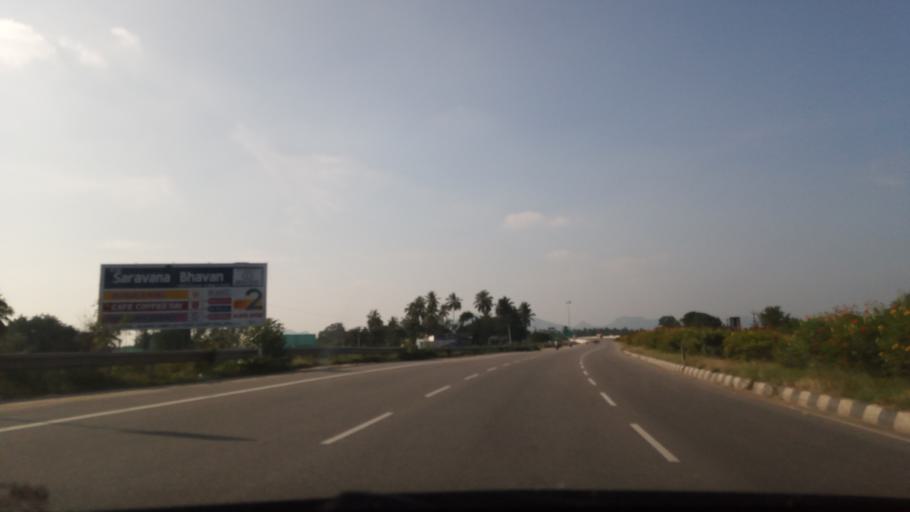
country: IN
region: Tamil Nadu
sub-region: Krishnagiri
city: Krishnagiri
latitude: 12.5711
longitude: 78.1712
